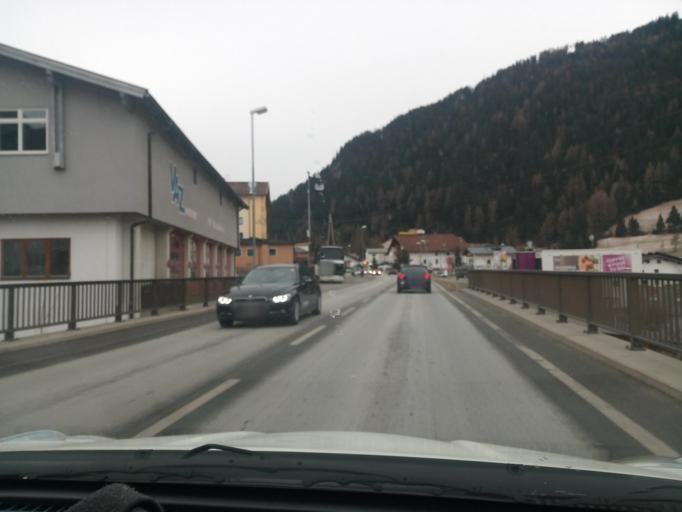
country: AT
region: Tyrol
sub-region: Politischer Bezirk Landeck
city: Nauders
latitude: 46.8926
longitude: 10.4987
